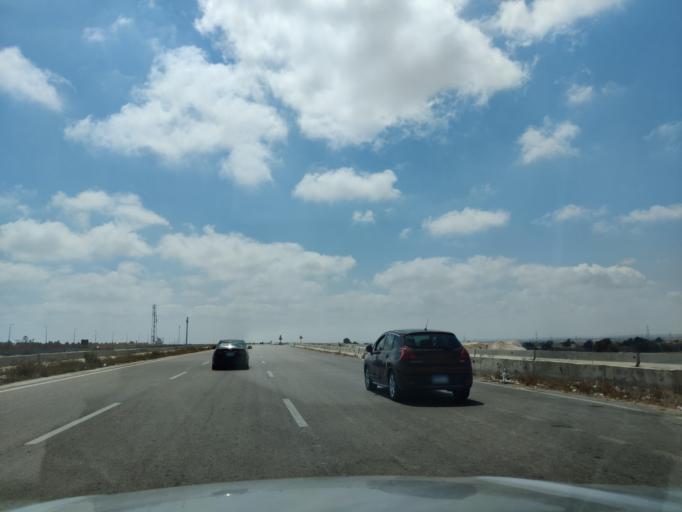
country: EG
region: Muhafazat Matruh
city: Al `Alamayn
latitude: 30.8155
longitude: 29.0358
